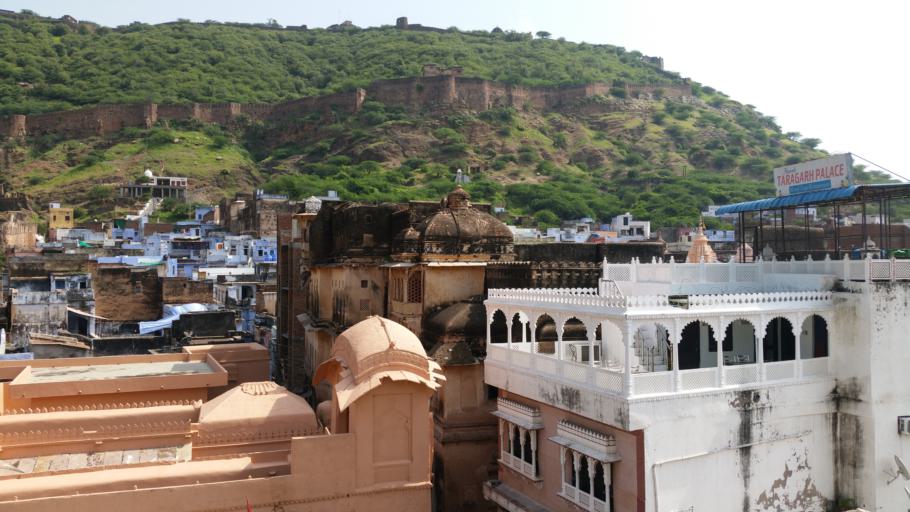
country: IN
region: Rajasthan
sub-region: Bundi
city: Bundi
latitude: 25.4468
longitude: 75.6363
